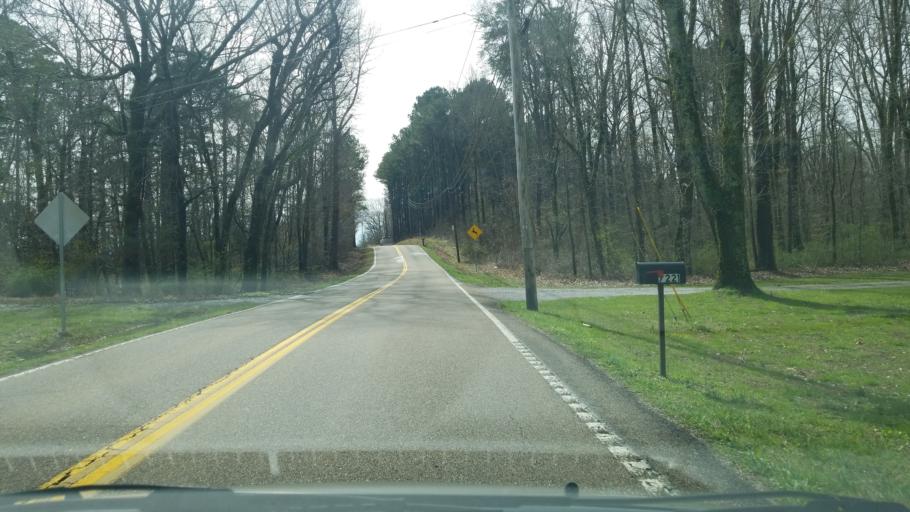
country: US
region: Tennessee
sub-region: Hamilton County
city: Harrison
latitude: 35.1315
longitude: -85.0701
